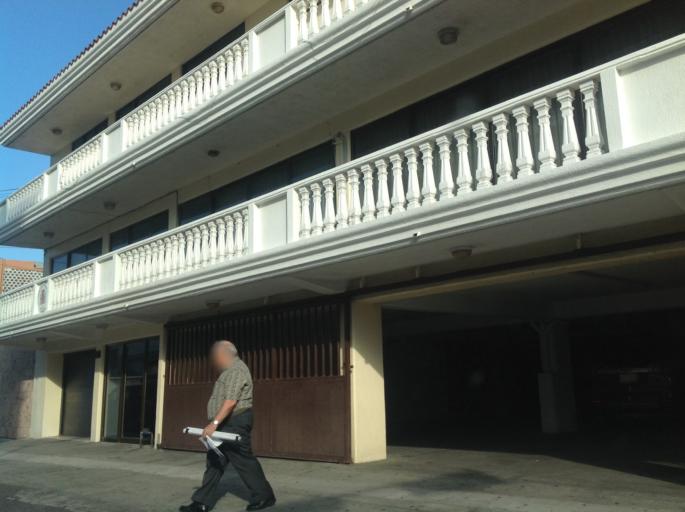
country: MX
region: Veracruz
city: Veracruz
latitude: 19.1989
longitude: -96.1332
